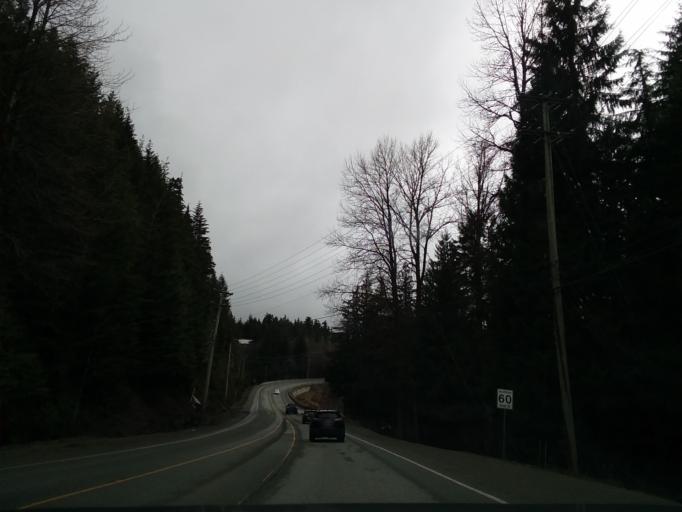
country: CA
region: British Columbia
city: Whistler
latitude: 50.1060
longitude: -122.9776
